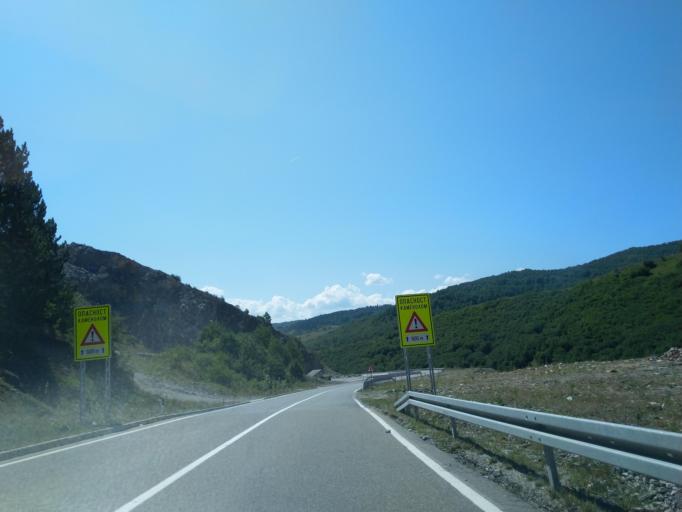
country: RS
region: Central Serbia
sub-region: Zlatiborski Okrug
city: Sjenica
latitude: 43.2988
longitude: 19.9365
